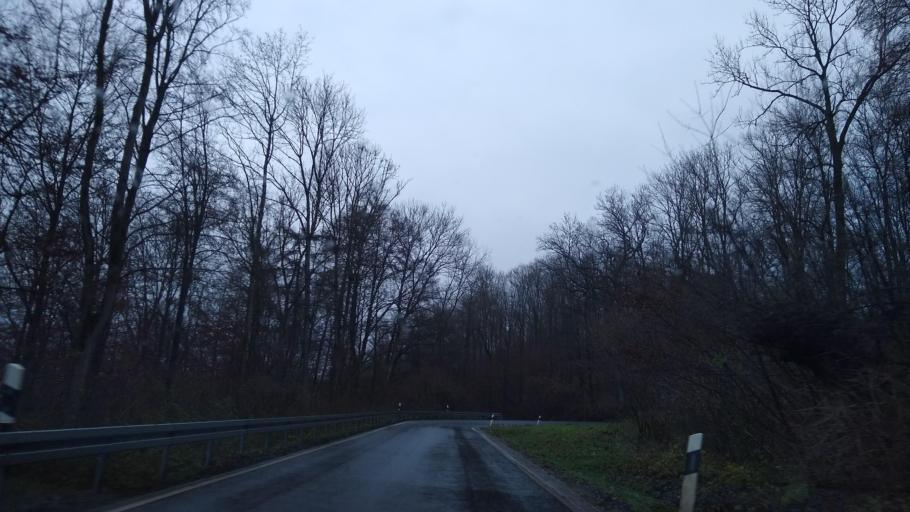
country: DE
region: Lower Saxony
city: Ottenstein
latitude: 51.9653
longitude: 9.4188
